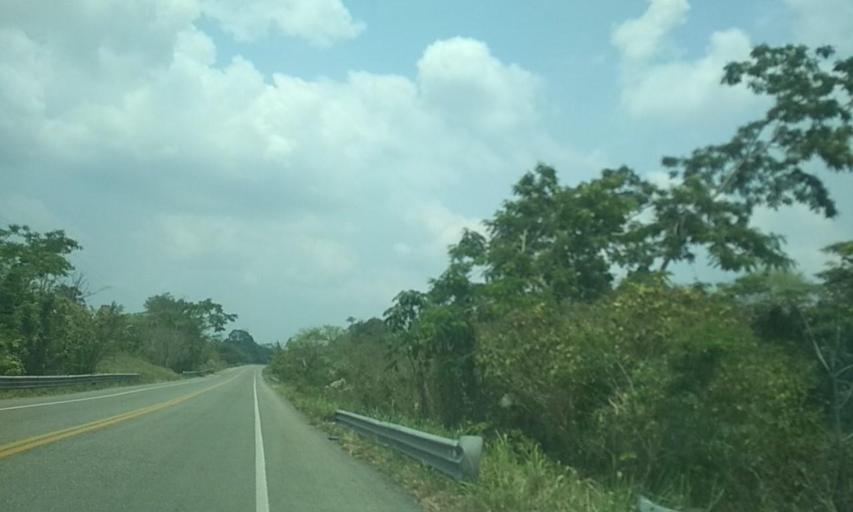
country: MX
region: Tabasco
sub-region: Huimanguillo
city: Francisco Rueda
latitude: 17.6474
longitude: -93.8315
